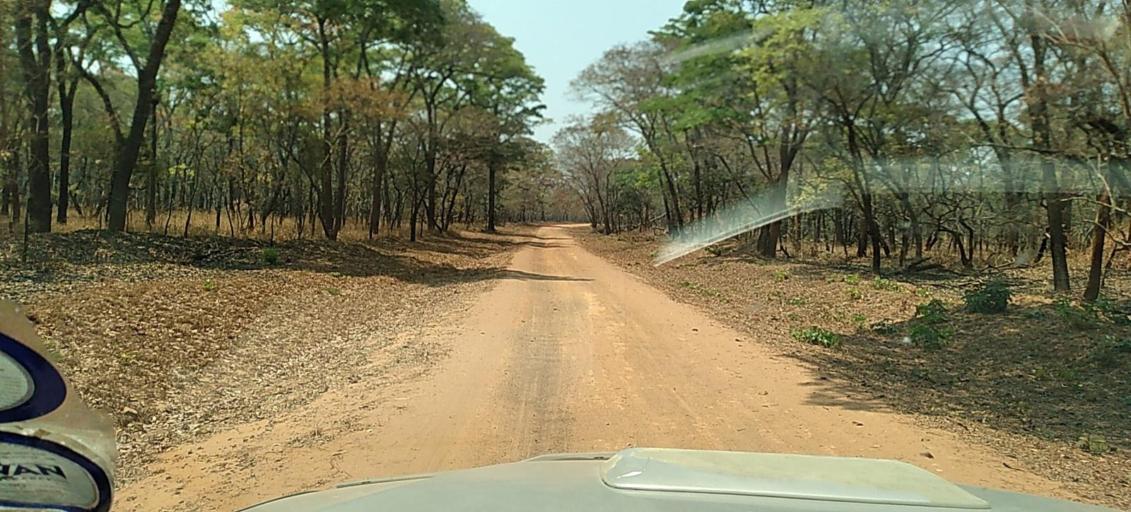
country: ZM
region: North-Western
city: Kasempa
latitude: -13.5564
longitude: 26.0709
